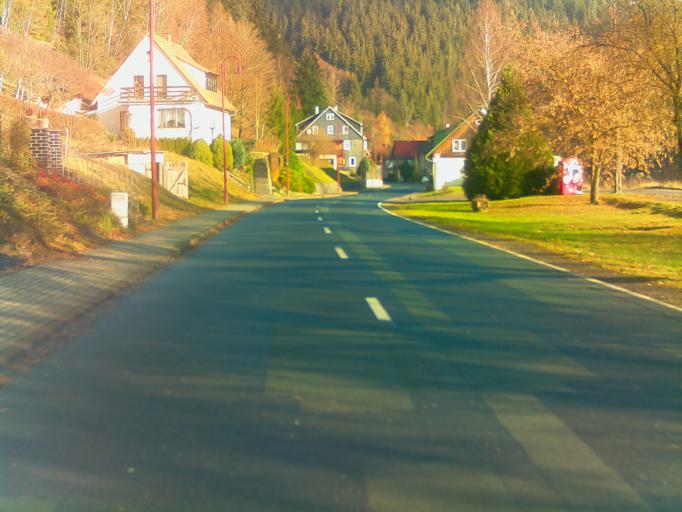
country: DE
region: Thuringia
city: Mellenbach-Glasbach
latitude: 50.6045
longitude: 11.1109
